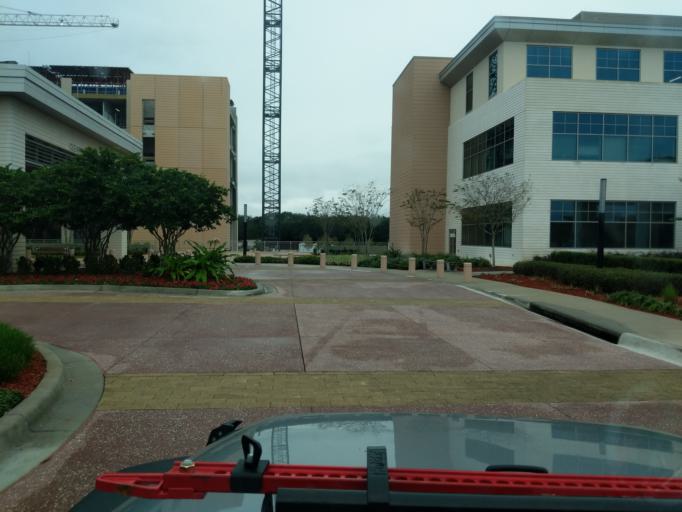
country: US
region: Florida
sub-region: Orange County
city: Winter Garden
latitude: 28.5246
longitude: -81.5893
